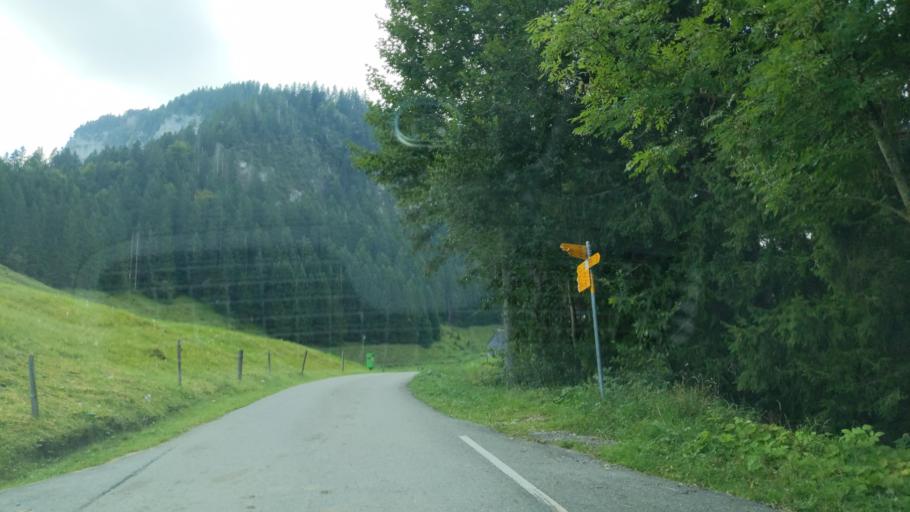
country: CH
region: Appenzell Innerrhoden
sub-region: Appenzell Inner Rhodes
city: Appenzell
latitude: 47.2939
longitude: 9.4175
